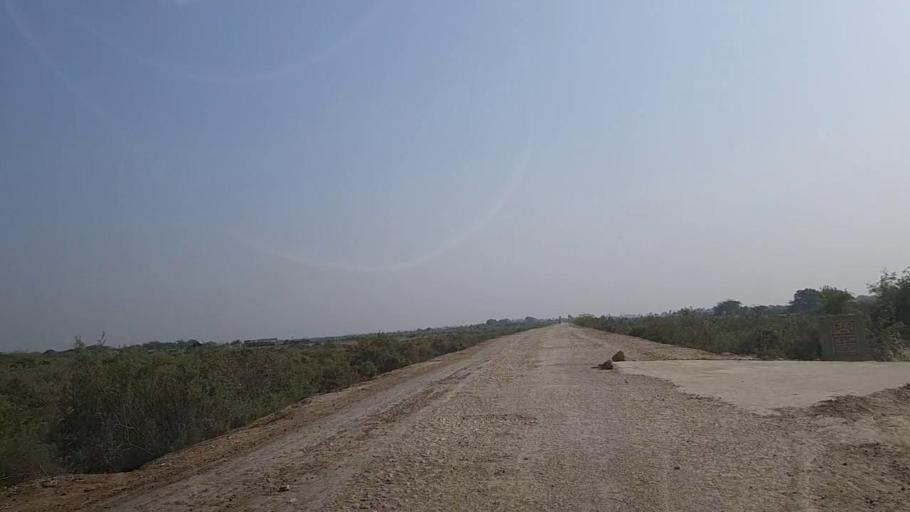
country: PK
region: Sindh
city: Keti Bandar
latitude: 24.2541
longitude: 67.6245
